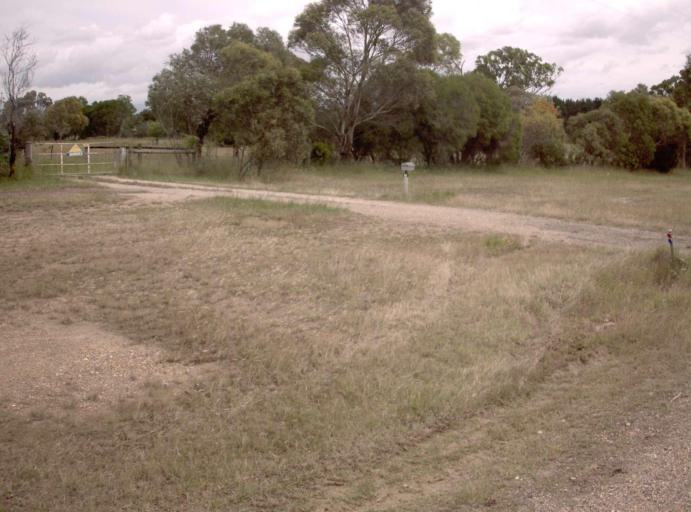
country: AU
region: Victoria
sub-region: Wellington
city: Sale
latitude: -37.9442
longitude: 147.0912
